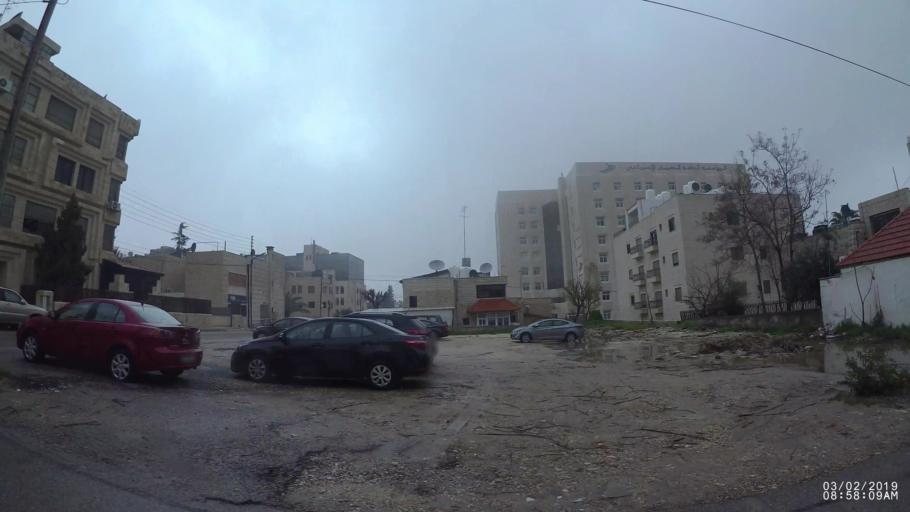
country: JO
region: Amman
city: Al Jubayhah
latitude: 31.9669
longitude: 35.8791
